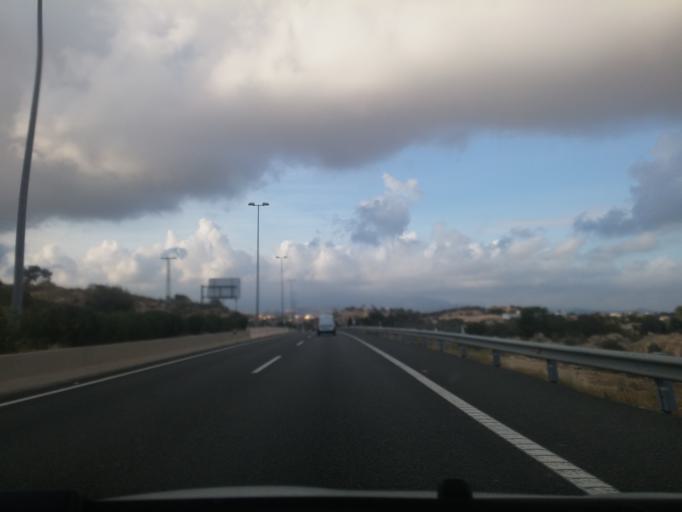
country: ES
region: Valencia
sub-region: Provincia de Alicante
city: San Juan de Alicante
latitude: 38.3930
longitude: -0.4514
